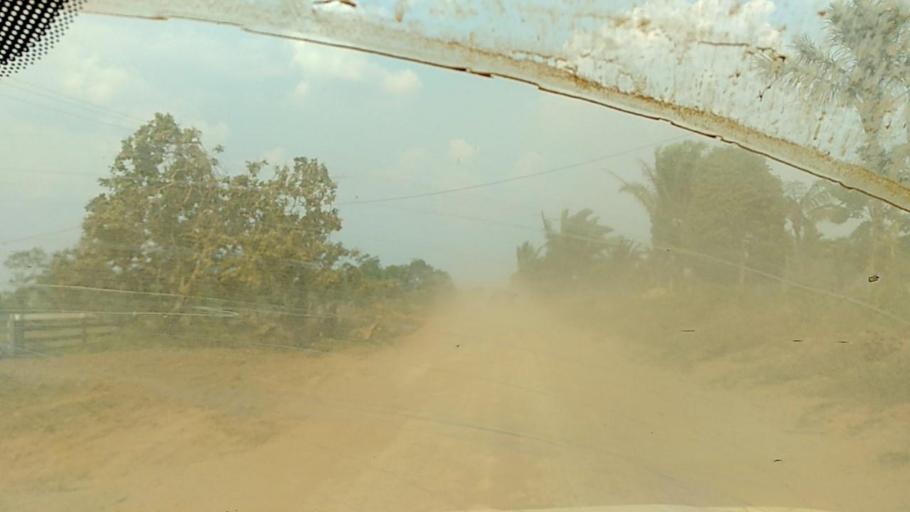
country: BR
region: Rondonia
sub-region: Porto Velho
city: Porto Velho
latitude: -8.6830
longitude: -63.2271
